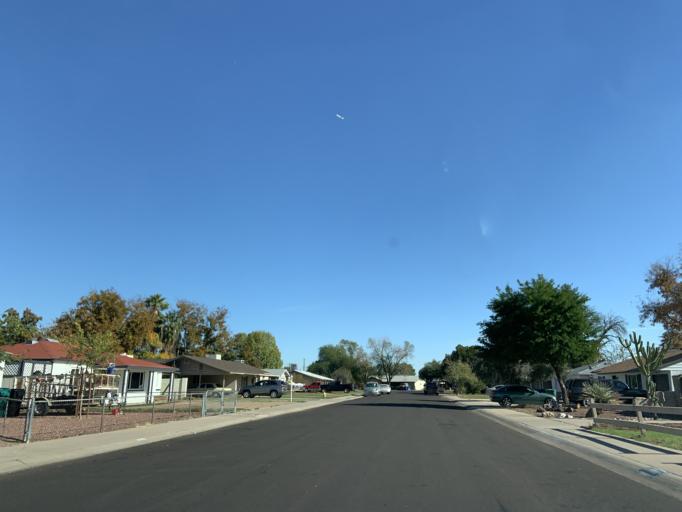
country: US
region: Arizona
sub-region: Maricopa County
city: Mesa
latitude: 33.4172
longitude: -111.8608
